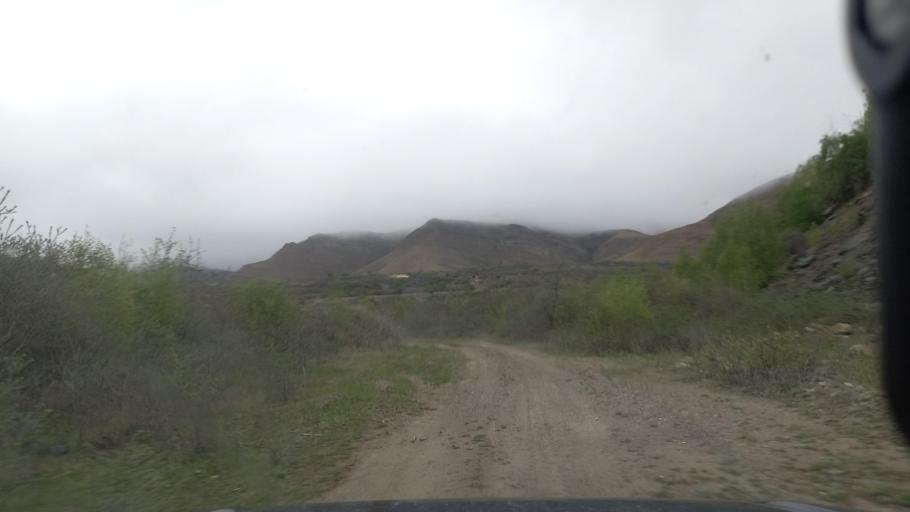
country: RU
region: Kabardino-Balkariya
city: Bylym
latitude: 43.4545
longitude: 43.0006
